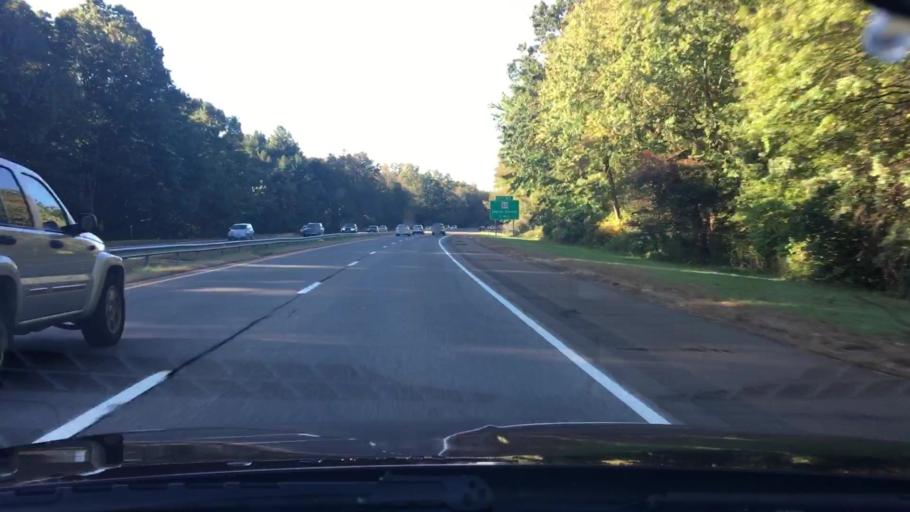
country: US
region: Connecticut
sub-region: New Haven County
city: North Haven
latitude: 41.4061
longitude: -72.8615
